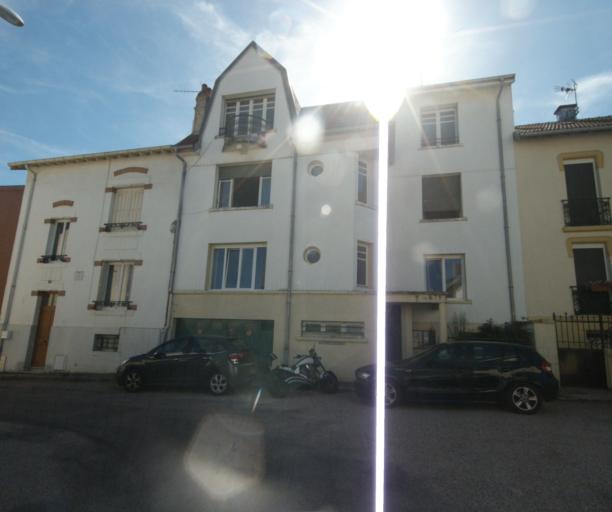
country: FR
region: Lorraine
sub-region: Departement des Vosges
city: Chantraine
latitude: 48.1780
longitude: 6.4372
